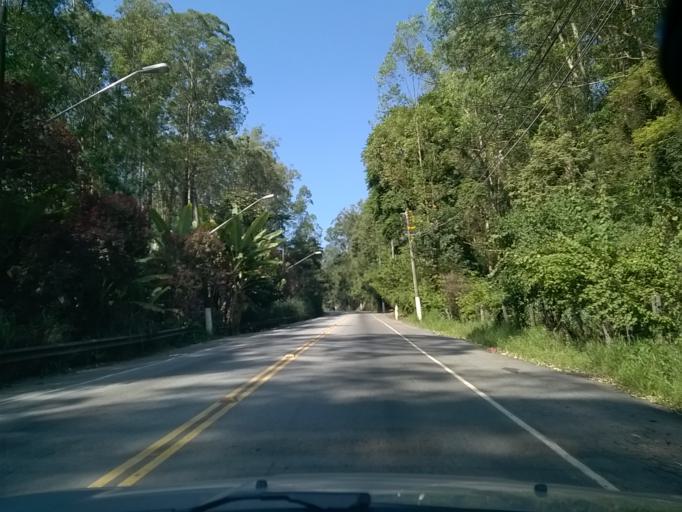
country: BR
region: Sao Paulo
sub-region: Caieiras
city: Caieiras
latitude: -23.4185
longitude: -46.7845
